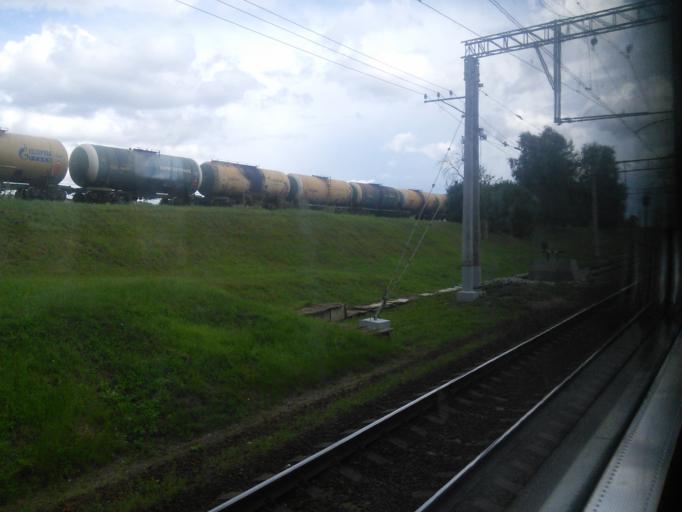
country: RU
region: Moscow
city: Lefortovo
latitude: 55.7697
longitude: 37.7180
